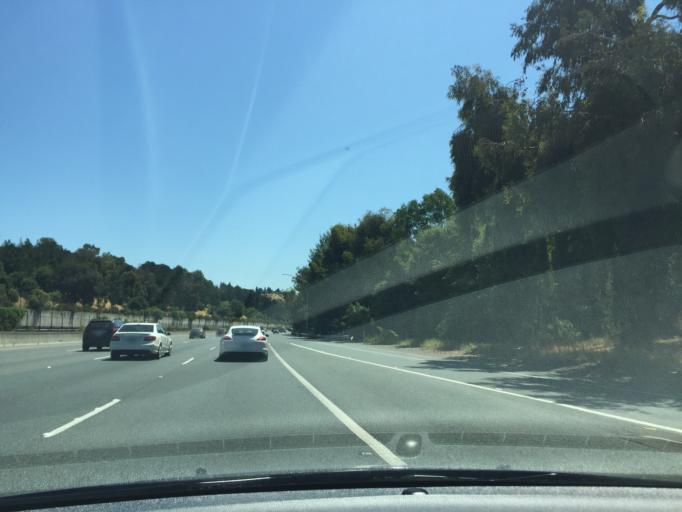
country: US
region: California
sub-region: Contra Costa County
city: Orinda
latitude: 37.8924
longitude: -122.1670
